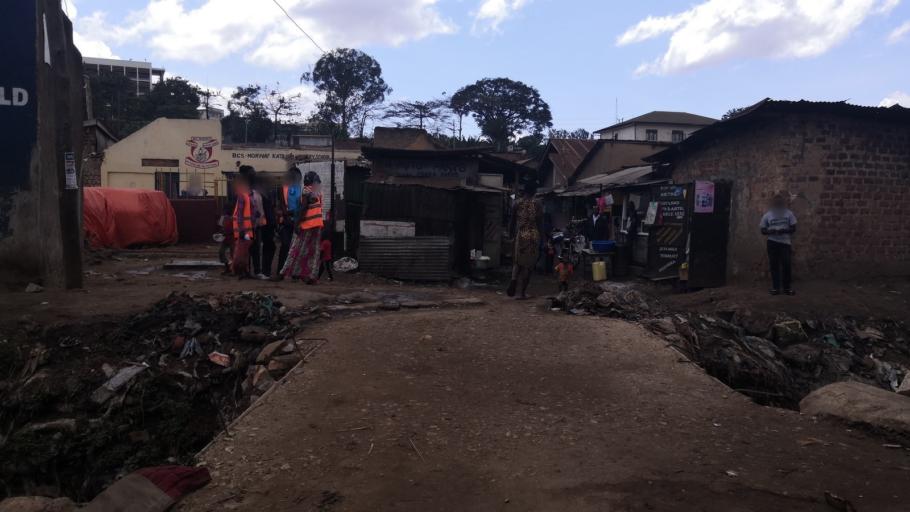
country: UG
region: Central Region
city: Kampala Central Division
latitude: 0.3360
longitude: 32.5742
